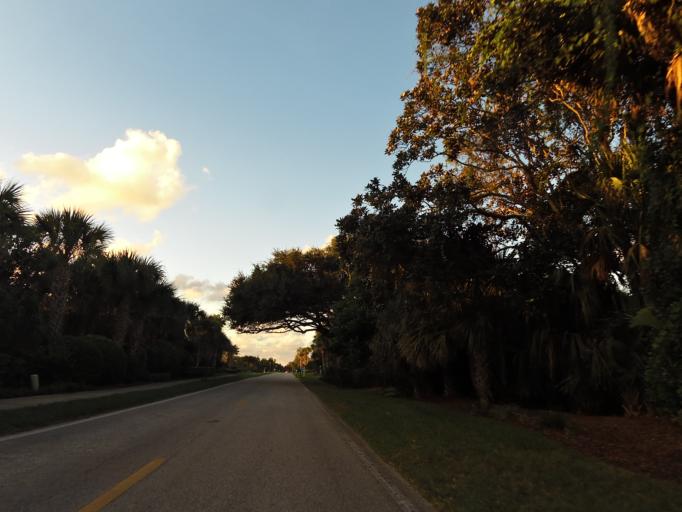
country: US
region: Florida
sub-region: Saint Johns County
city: Sawgrass
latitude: 30.1685
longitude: -81.3589
